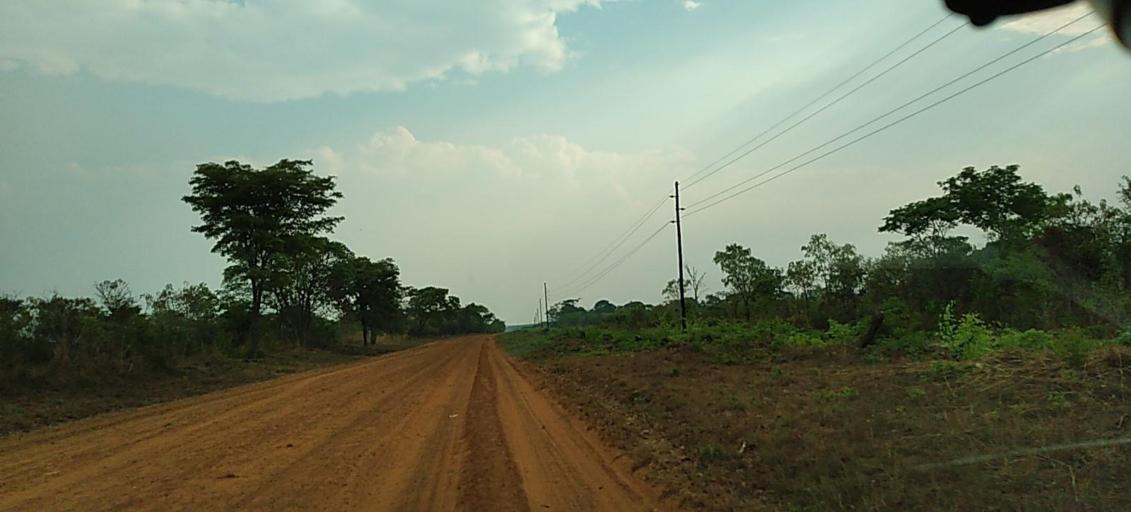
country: ZM
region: North-Western
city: Kabompo
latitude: -13.9001
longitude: 23.6560
